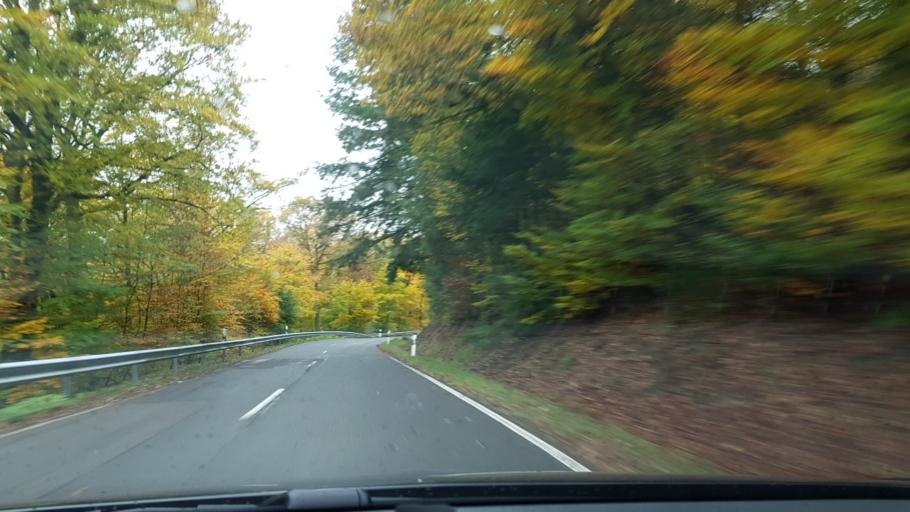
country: DE
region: Rheinland-Pfalz
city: Fell
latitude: 49.7719
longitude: 6.8144
